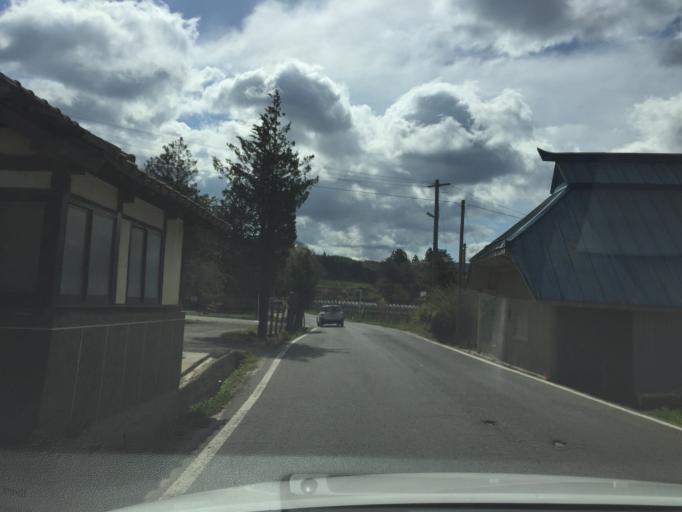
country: JP
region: Fukushima
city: Funehikimachi-funehiki
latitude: 37.5998
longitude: 140.6774
